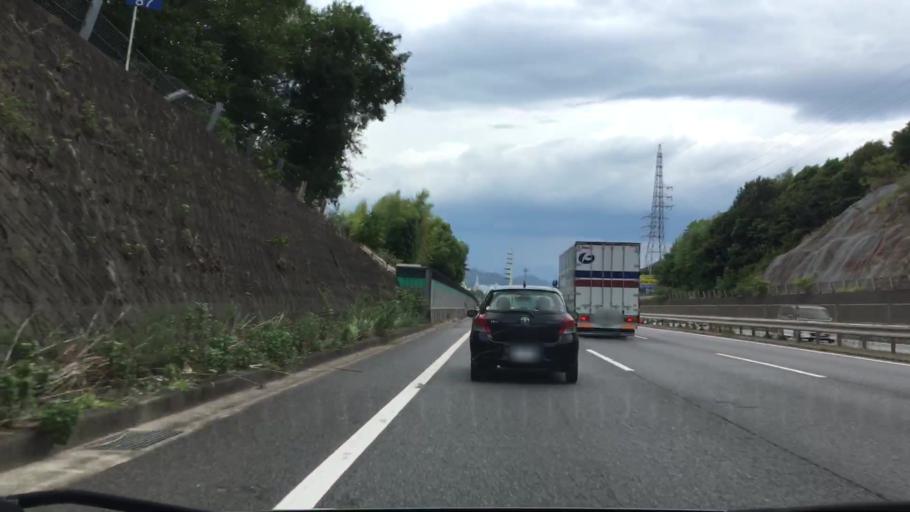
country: JP
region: Hyogo
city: Himeji
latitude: 34.8029
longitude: 134.7062
